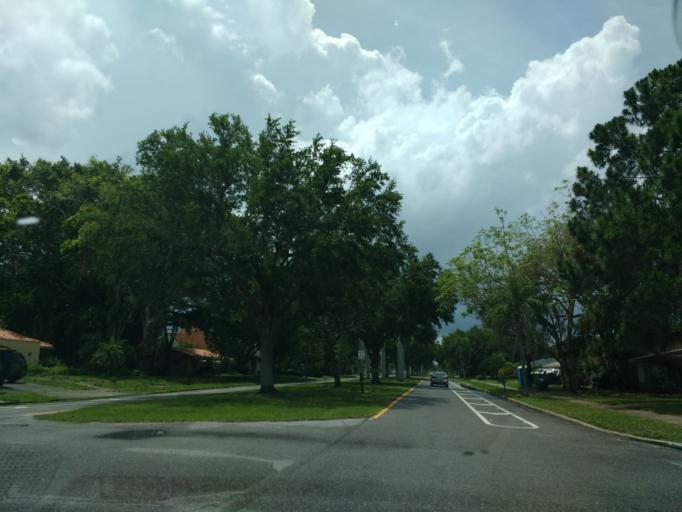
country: US
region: Florida
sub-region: Sarasota County
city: Venice
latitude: 27.0932
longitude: -82.4502
